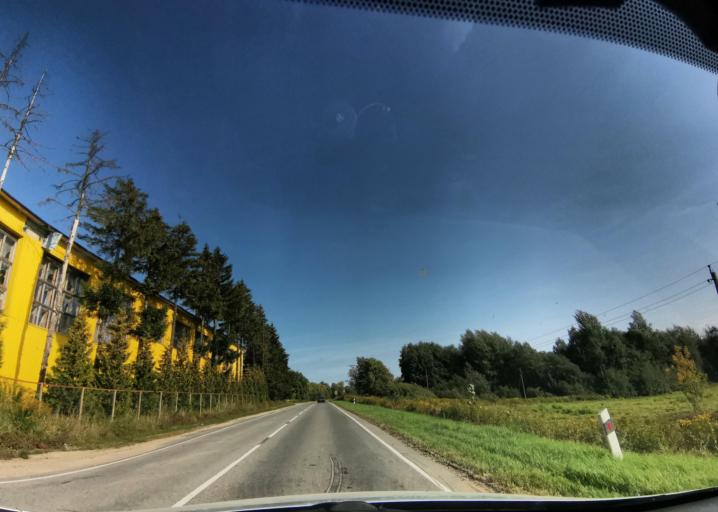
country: RU
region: Kaliningrad
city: Neman
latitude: 55.0186
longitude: 22.0981
